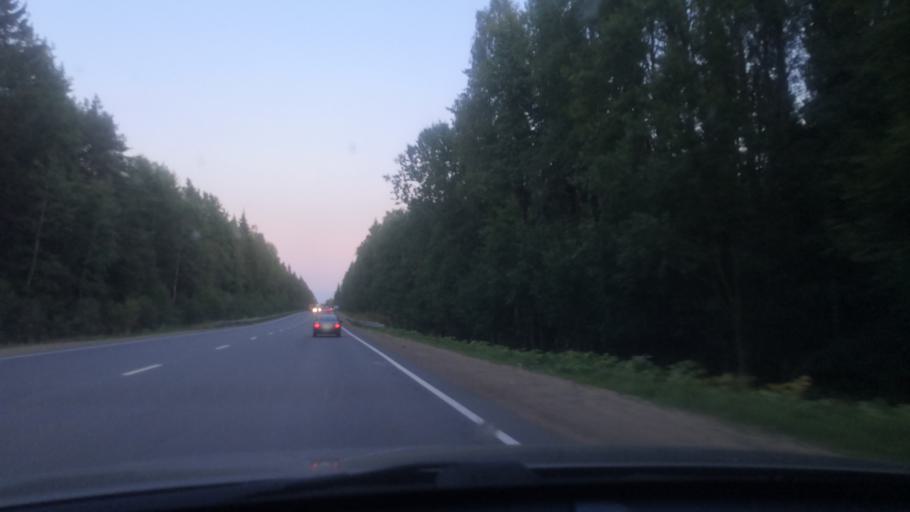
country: RU
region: St.-Petersburg
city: Pesochnyy
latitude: 60.1857
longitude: 30.1136
